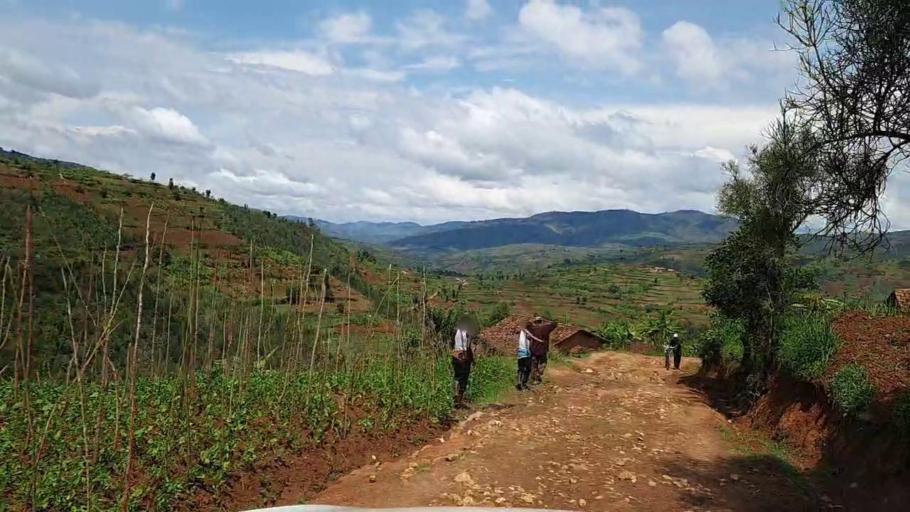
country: RW
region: Southern Province
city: Gikongoro
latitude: -2.3587
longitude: 29.5488
